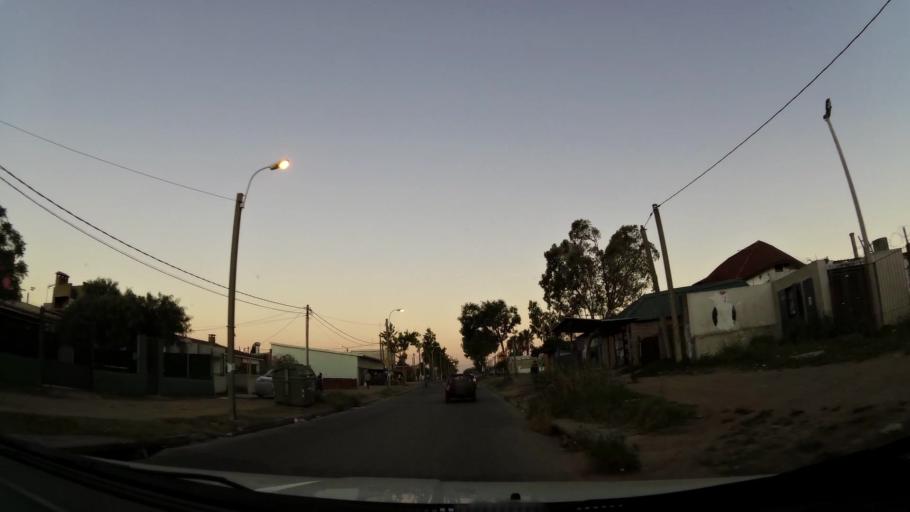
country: UY
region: Canelones
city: Toledo
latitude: -34.8176
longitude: -56.1436
